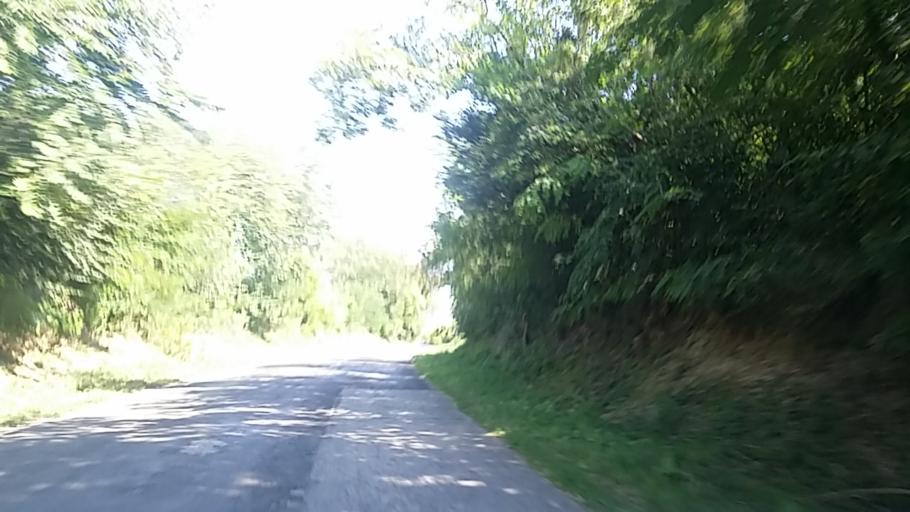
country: HU
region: Tolna
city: Hogyesz
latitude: 46.5217
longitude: 18.4196
